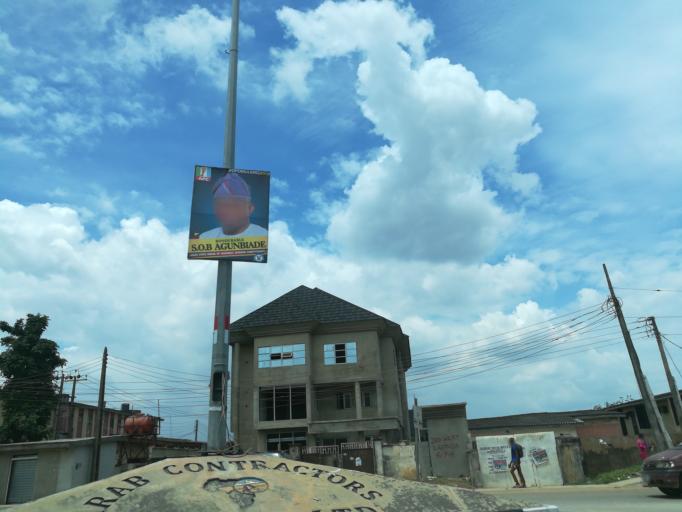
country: NG
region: Lagos
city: Ebute Ikorodu
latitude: 6.6005
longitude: 3.4932
